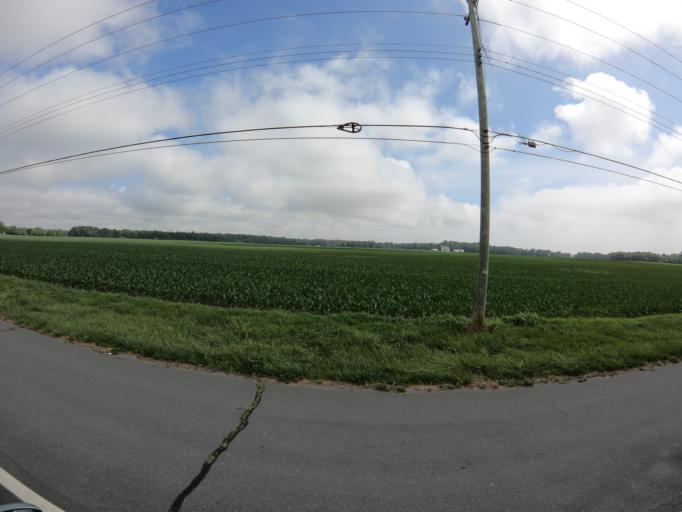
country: US
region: Delaware
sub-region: Kent County
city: Riverview
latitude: 39.0087
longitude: -75.4797
